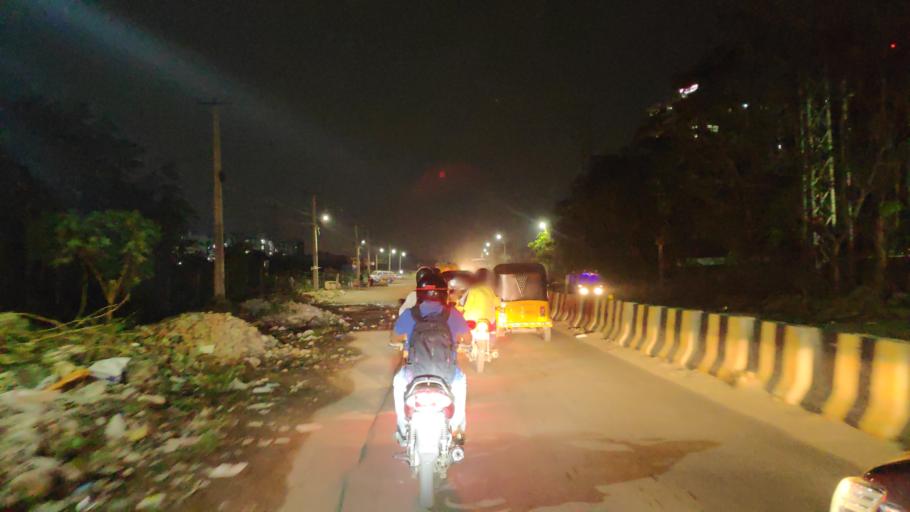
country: IN
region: Telangana
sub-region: Rangareddi
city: Kukatpalli
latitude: 17.4760
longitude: 78.3802
